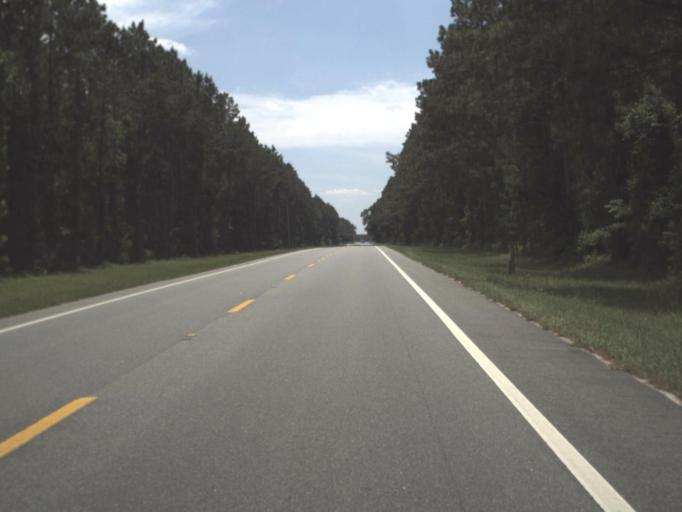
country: US
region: Florida
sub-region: Calhoun County
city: Blountstown
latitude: 30.3194
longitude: -85.1276
